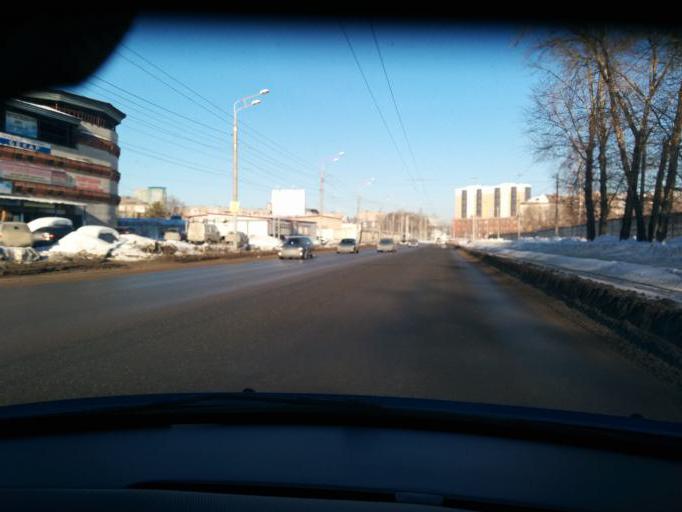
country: RU
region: Perm
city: Perm
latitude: 57.9943
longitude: 56.2593
